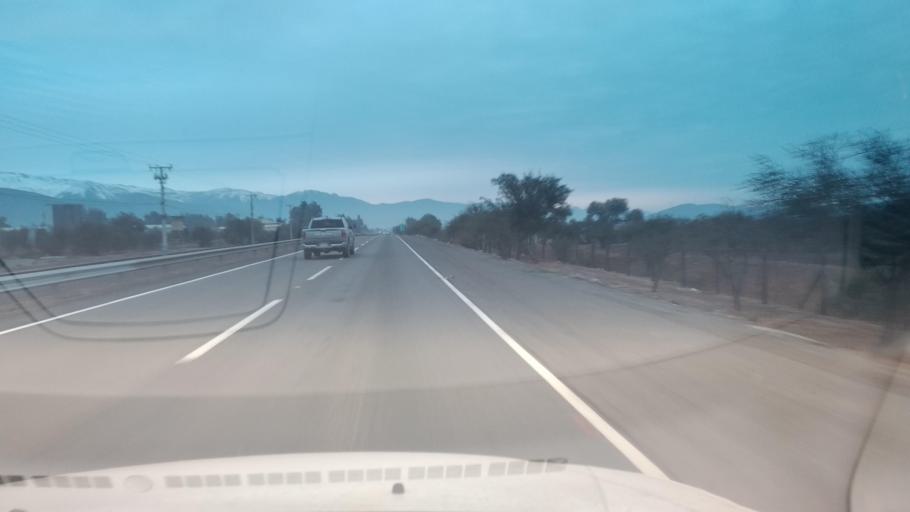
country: CL
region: Santiago Metropolitan
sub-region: Provincia de Chacabuco
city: Chicureo Abajo
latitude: -33.1332
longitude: -70.6685
